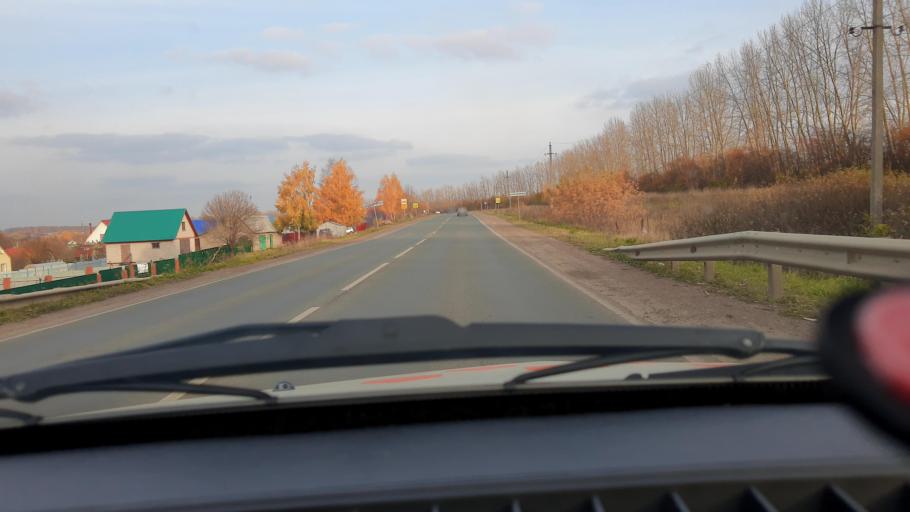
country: RU
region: Bashkortostan
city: Iglino
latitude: 54.7930
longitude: 56.2796
